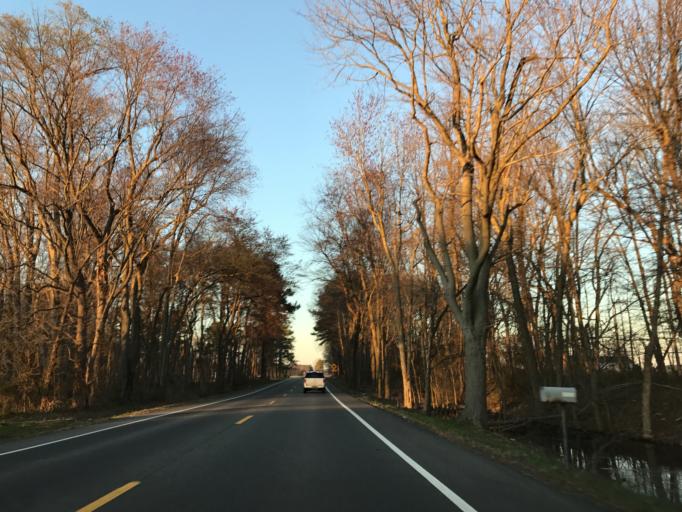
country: US
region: Maryland
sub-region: Talbot County
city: Easton
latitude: 38.8371
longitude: -76.0280
